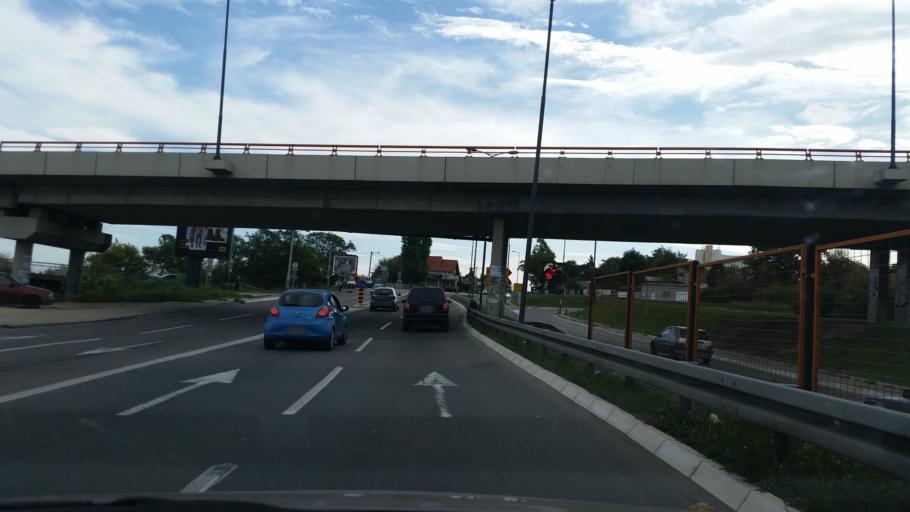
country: RS
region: Central Serbia
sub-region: Belgrade
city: Palilula
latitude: 44.8180
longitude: 20.4898
